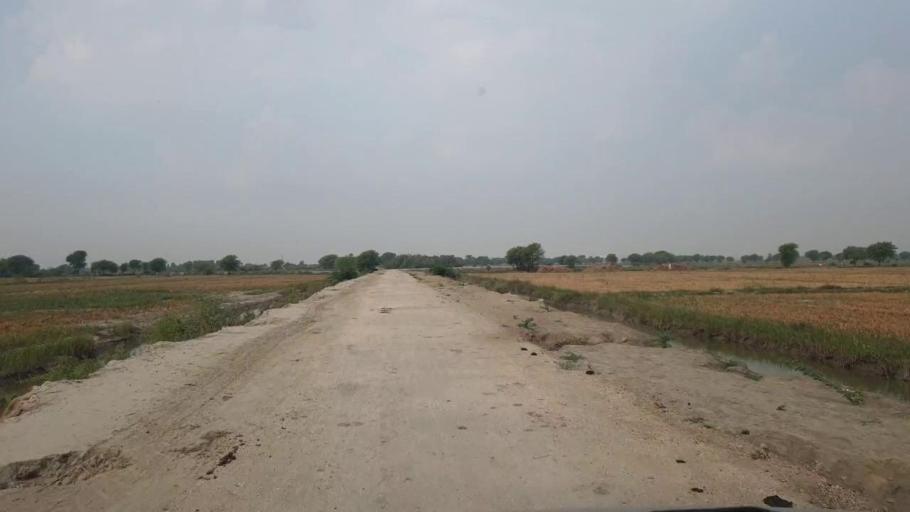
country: PK
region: Sindh
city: Talhar
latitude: 24.8618
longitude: 68.8249
